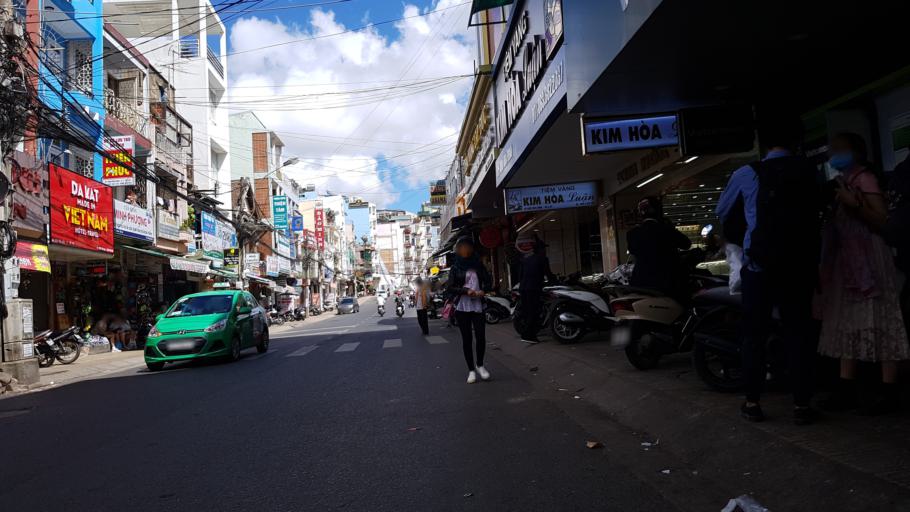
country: VN
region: Lam Dong
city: Da Lat
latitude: 11.9439
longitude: 108.4365
